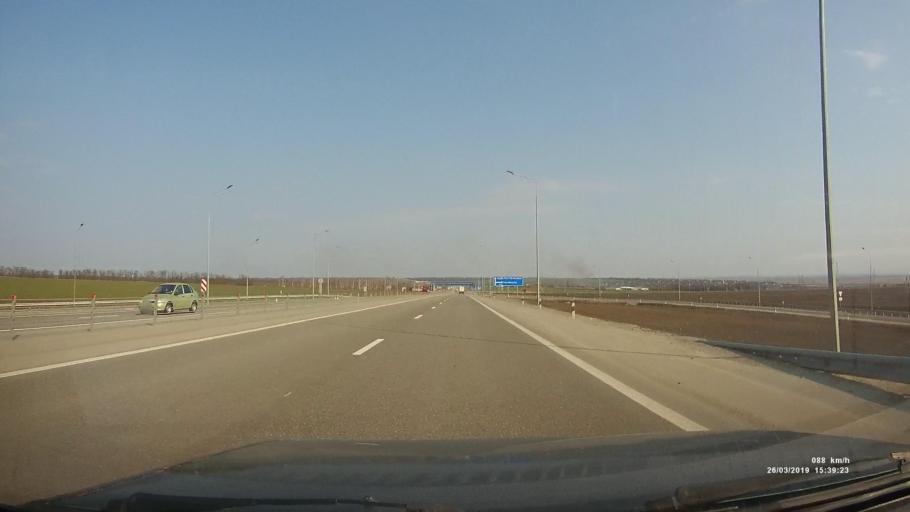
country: RU
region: Rostov
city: Sinyavskoye
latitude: 47.2939
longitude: 39.2842
